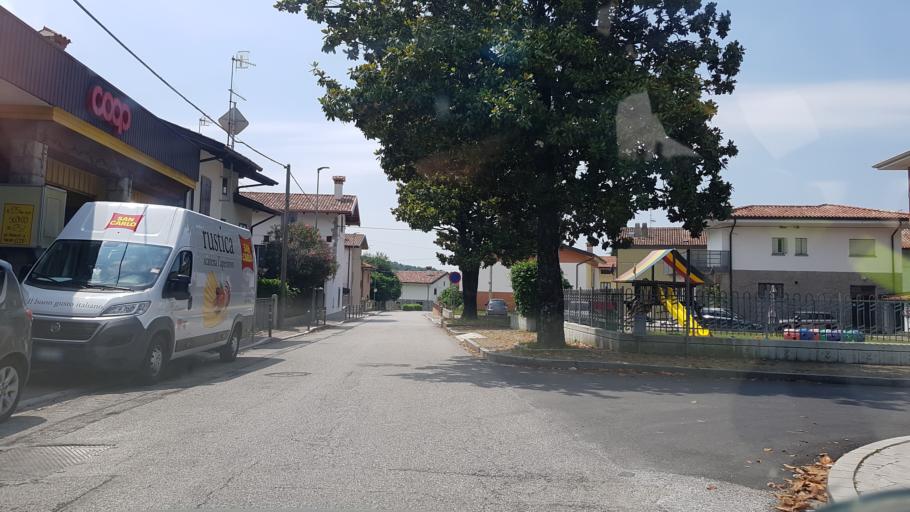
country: IT
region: Friuli Venezia Giulia
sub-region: Provincia di Udine
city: Torreano
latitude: 46.1297
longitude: 13.4324
